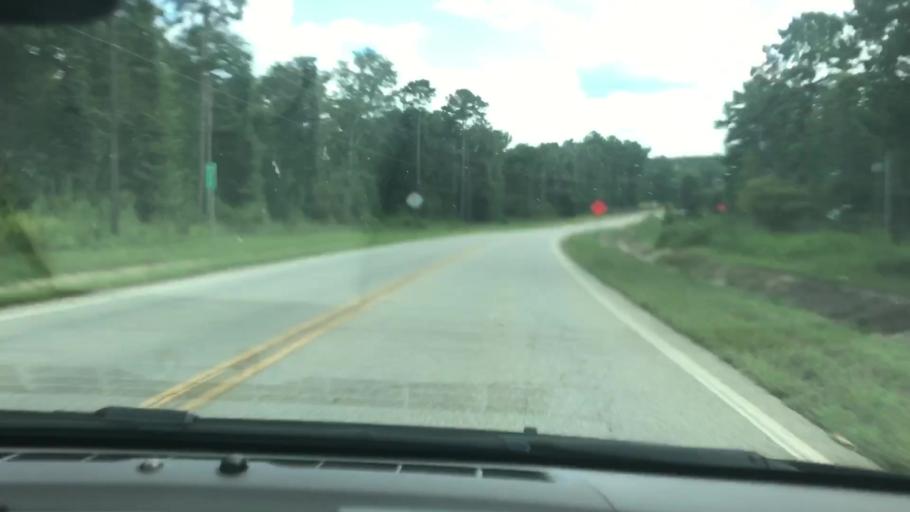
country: US
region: Georgia
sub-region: Quitman County
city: Georgetown
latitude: 31.7524
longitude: -85.0565
